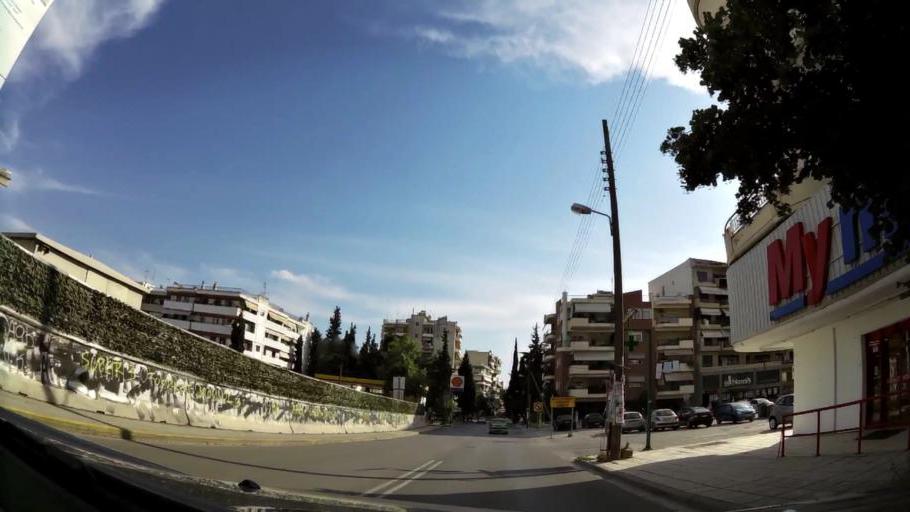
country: GR
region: Central Macedonia
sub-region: Nomos Thessalonikis
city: Kalamaria
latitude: 40.5726
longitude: 22.9609
